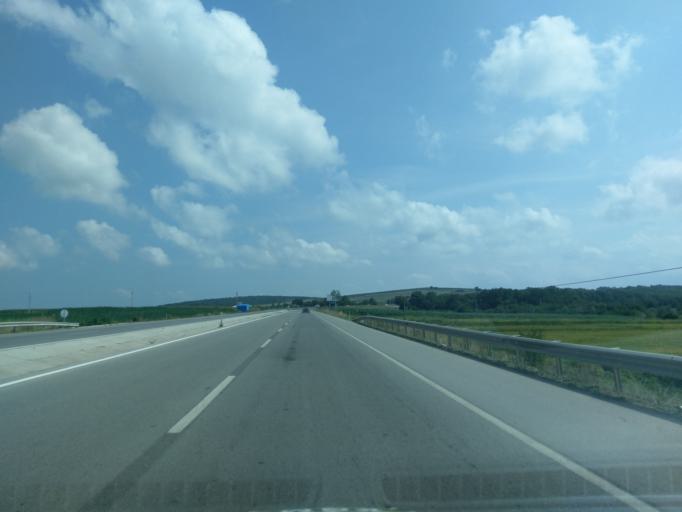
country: TR
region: Samsun
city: Bafra
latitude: 41.6024
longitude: 35.8251
